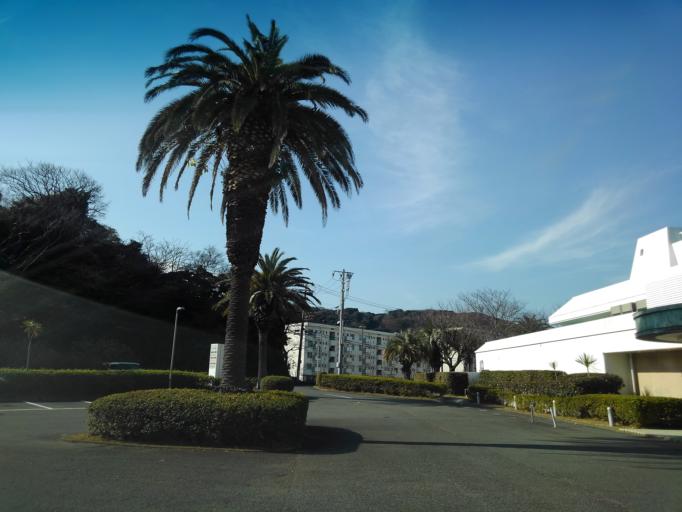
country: JP
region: Kanagawa
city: Yokosuka
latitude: 35.2611
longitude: 139.7382
